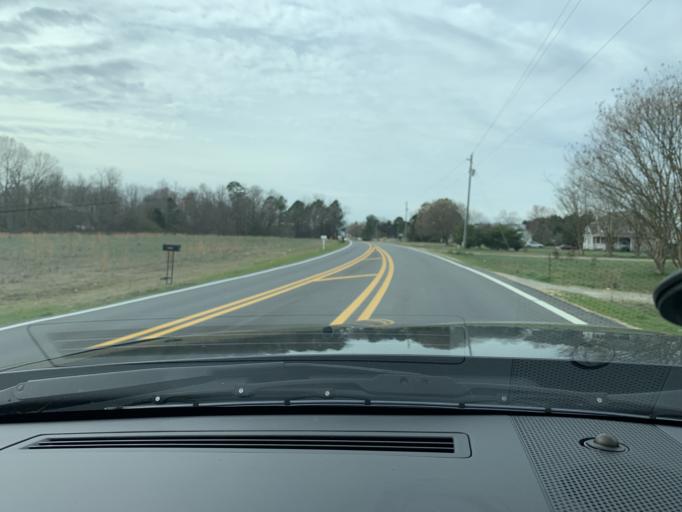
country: US
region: North Carolina
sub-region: Johnston County
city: Wilsons Mills
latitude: 35.6209
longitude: -78.4000
